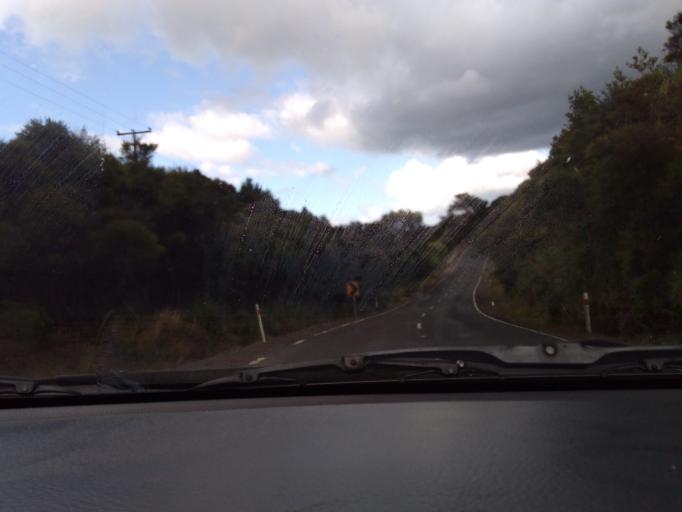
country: NZ
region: Auckland
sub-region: Auckland
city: Titirangi
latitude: -37.0043
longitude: 174.5870
